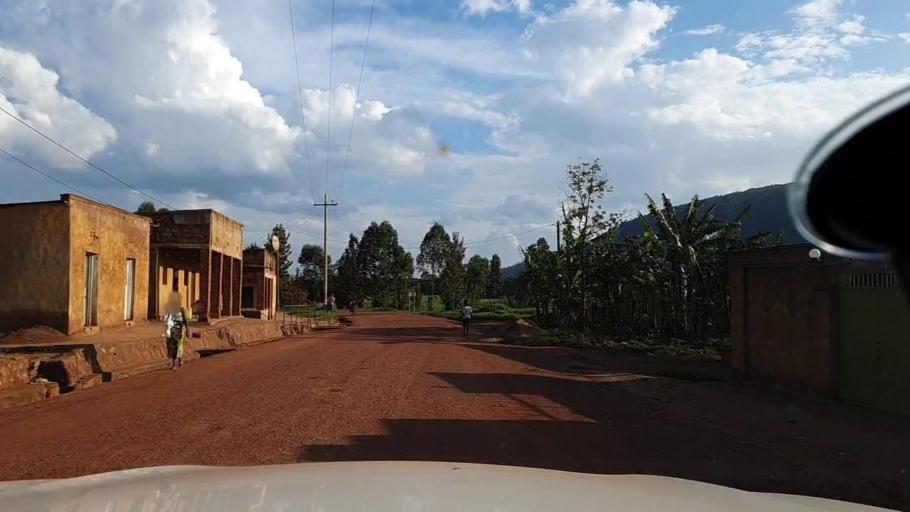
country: RW
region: Kigali
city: Kigali
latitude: -1.9074
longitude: 29.9803
